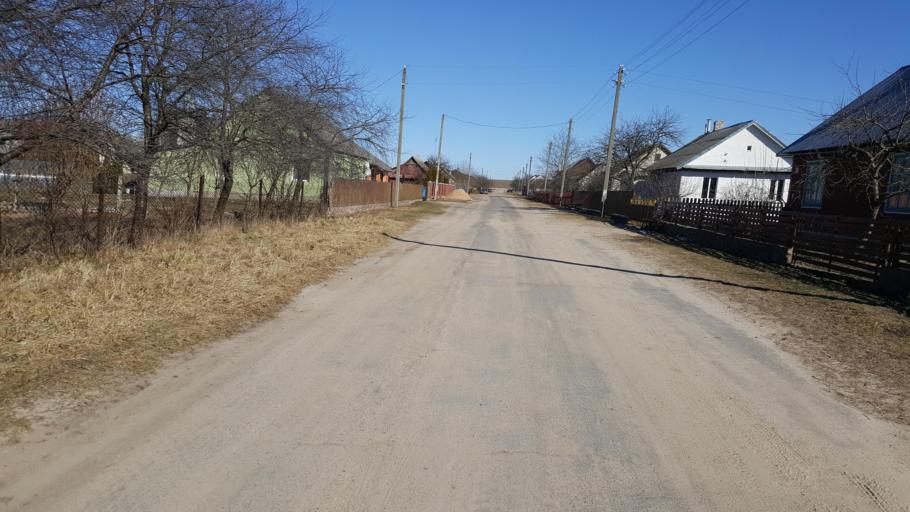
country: BY
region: Brest
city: Kamyanyets
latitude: 52.4088
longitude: 23.8303
